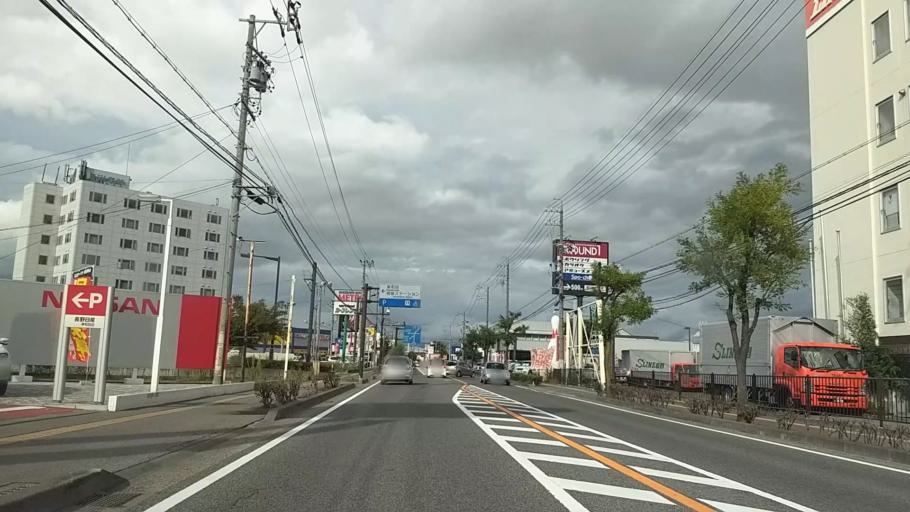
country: JP
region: Nagano
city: Nagano-shi
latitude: 36.6513
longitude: 138.2238
